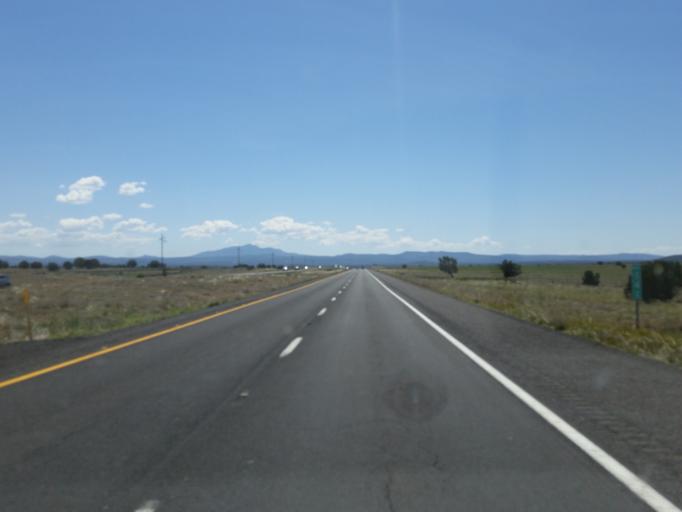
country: US
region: Arizona
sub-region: Yavapai County
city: Paulden
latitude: 35.2255
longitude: -112.5662
